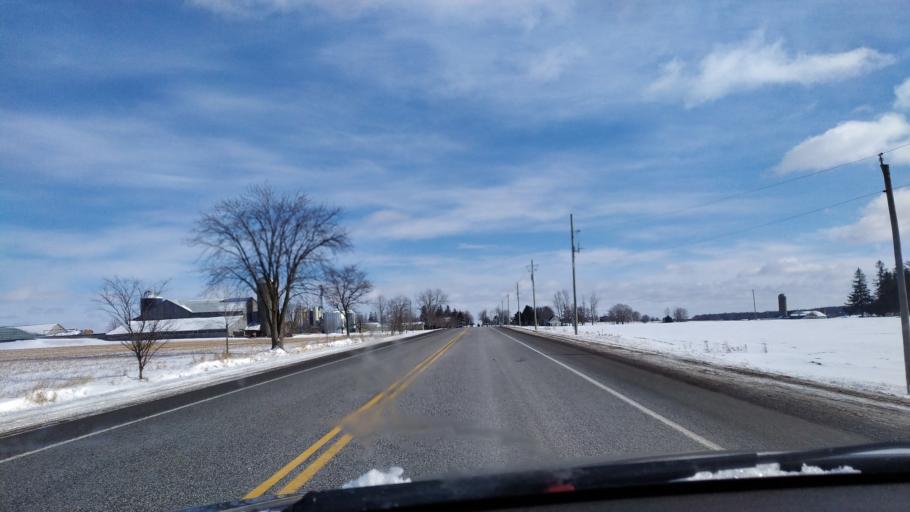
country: CA
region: Ontario
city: Waterloo
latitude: 43.5243
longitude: -80.6678
